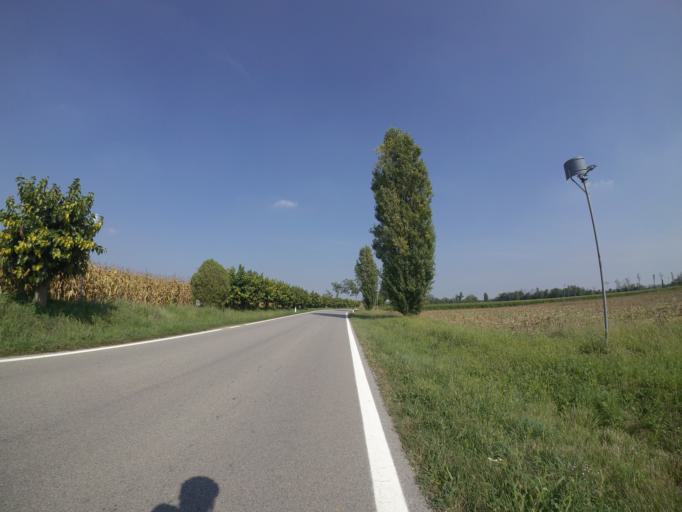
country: IT
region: Friuli Venezia Giulia
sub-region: Provincia di Udine
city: Basiliano
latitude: 46.0133
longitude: 13.0780
